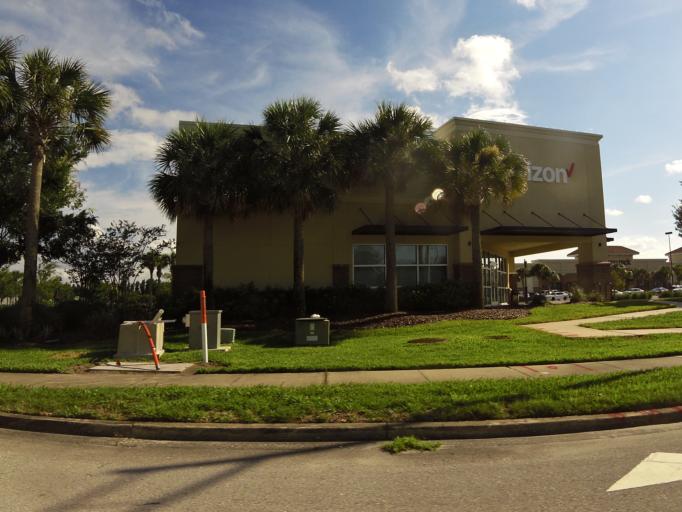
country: US
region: Florida
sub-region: Duval County
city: Jacksonville Beach
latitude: 30.2527
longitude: -81.5288
